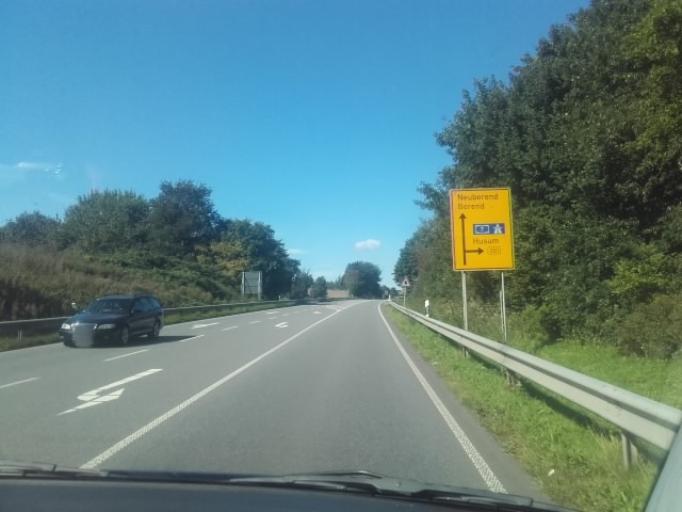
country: DE
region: Schleswig-Holstein
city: Schleswig
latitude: 54.5355
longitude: 9.5579
